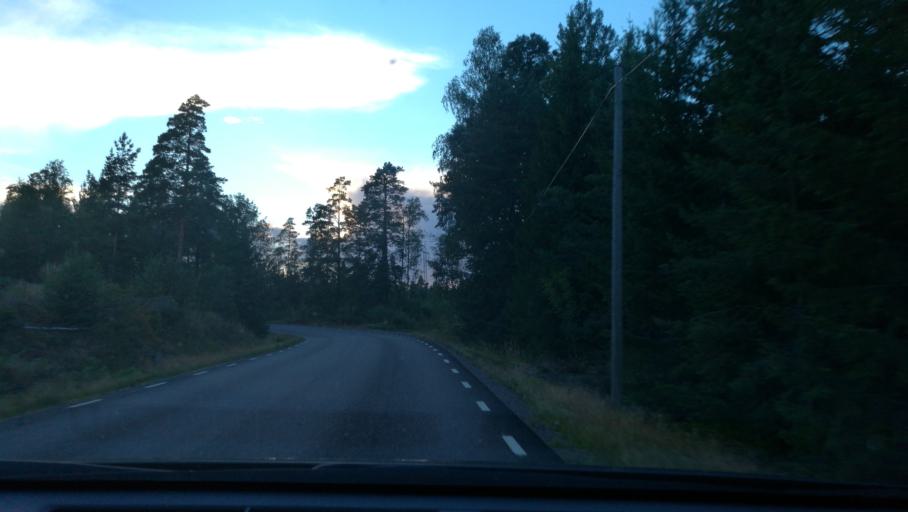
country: SE
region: OEstergoetland
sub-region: Norrkopings Kommun
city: Jursla
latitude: 58.8014
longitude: 16.1433
